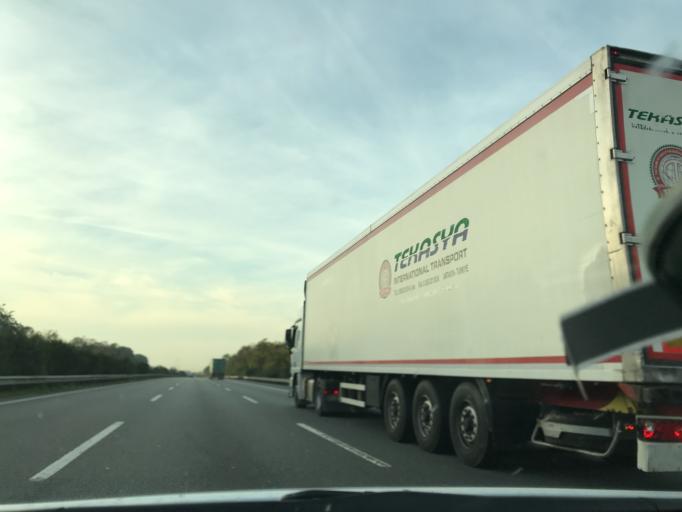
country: TR
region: Duzce
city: Cilimli
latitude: 40.8208
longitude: 31.0700
